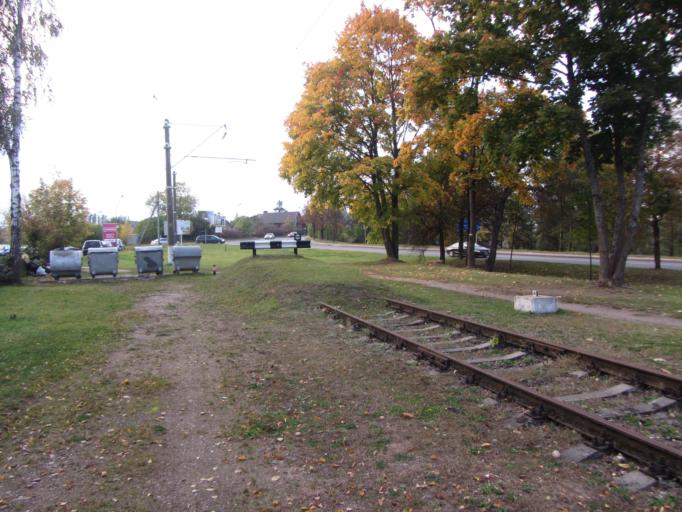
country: LT
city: Trakai
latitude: 54.6292
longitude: 24.9369
